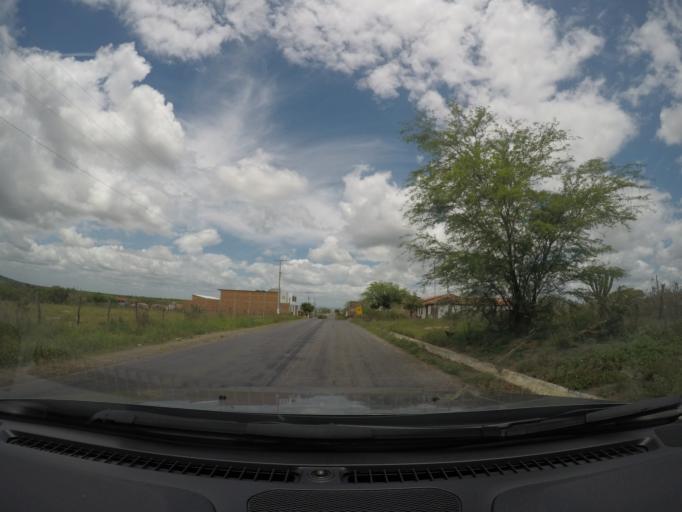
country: BR
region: Bahia
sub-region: Ipira
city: Ipira
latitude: -12.3040
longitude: -39.8979
